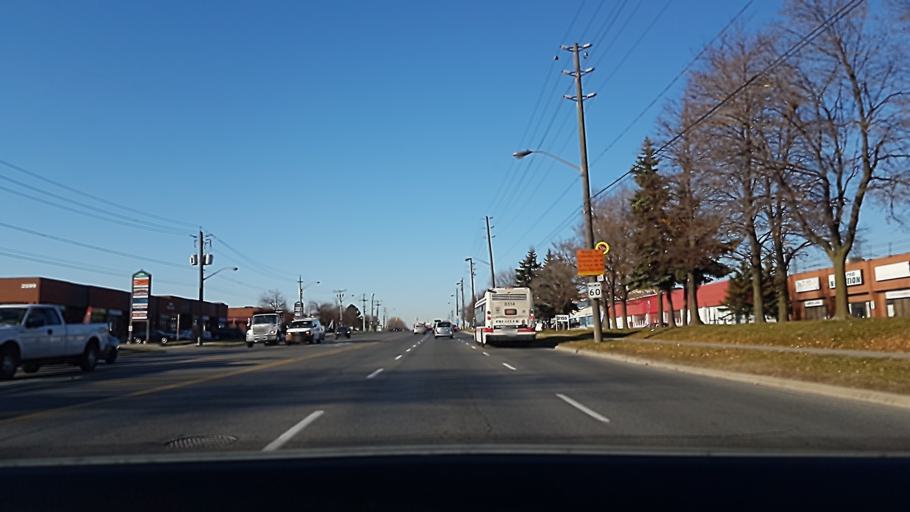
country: CA
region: Ontario
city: Concord
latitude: 43.7826
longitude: -79.4906
